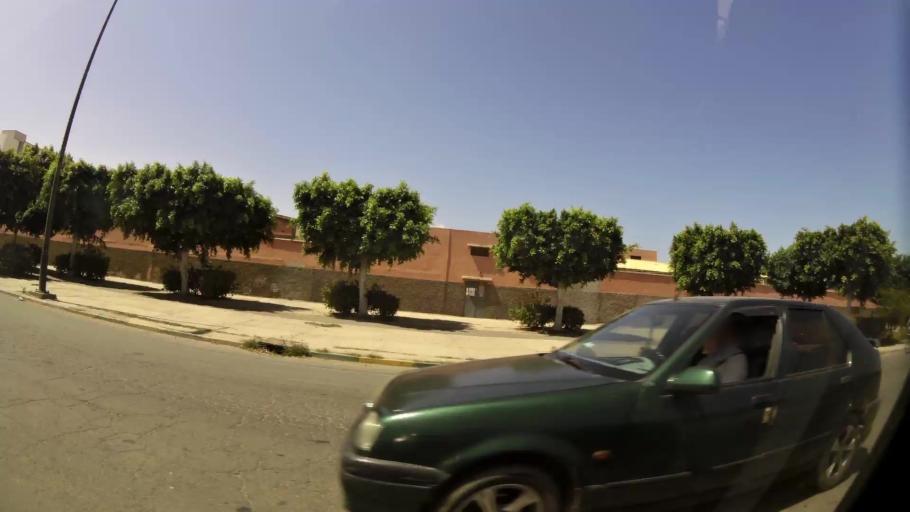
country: MA
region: Souss-Massa-Draa
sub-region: Inezgane-Ait Mellou
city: Inezgane
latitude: 30.3271
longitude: -9.4856
